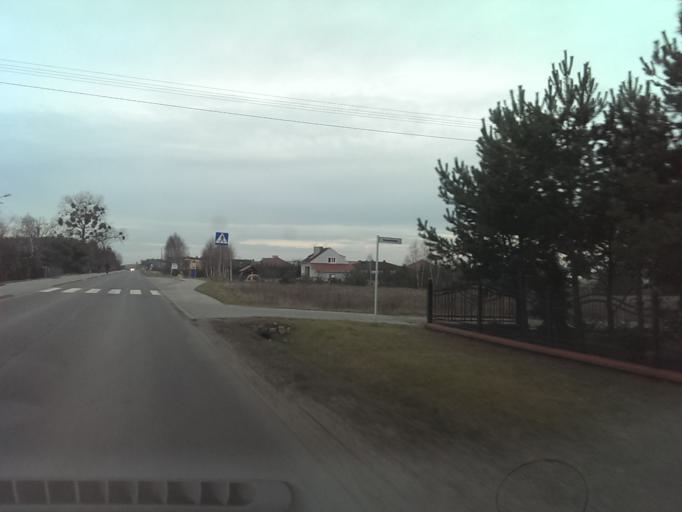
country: PL
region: Kujawsko-Pomorskie
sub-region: Powiat nakielski
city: Szubin
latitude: 53.0756
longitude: 17.8012
